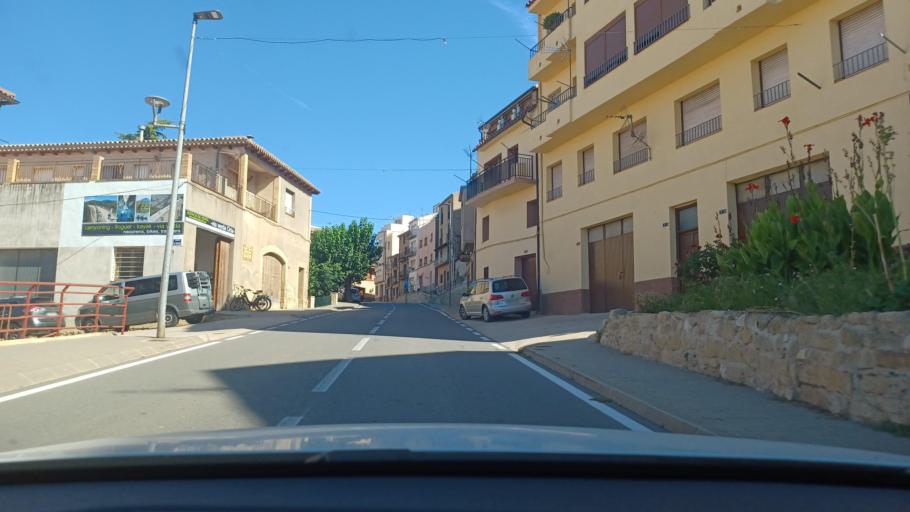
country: ES
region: Catalonia
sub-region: Provincia de Tarragona
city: Horta de Sant Joan
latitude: 40.9541
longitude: 0.3150
